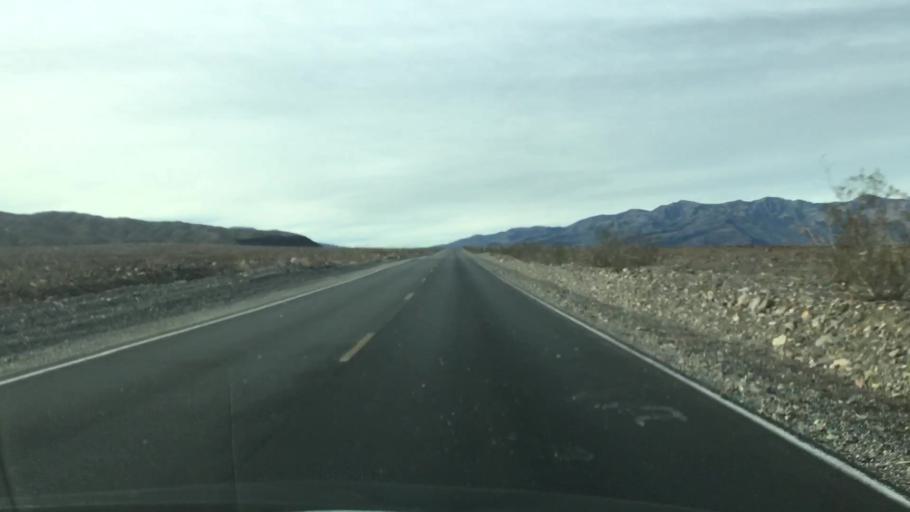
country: US
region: Nevada
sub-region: Nye County
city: Beatty
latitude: 36.5613
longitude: -117.2010
